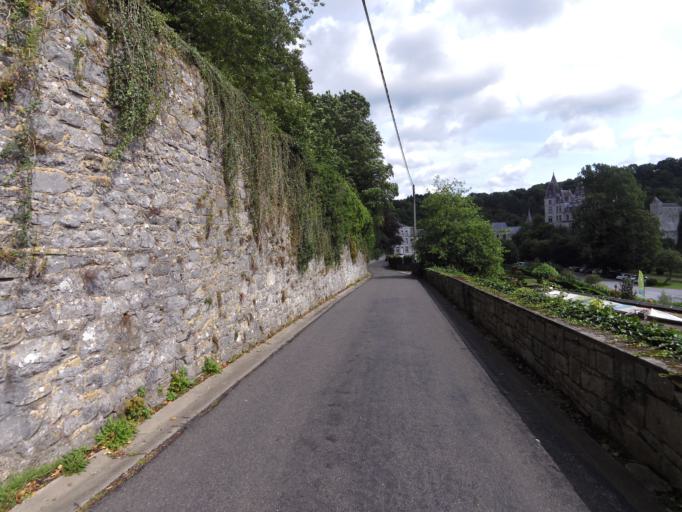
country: BE
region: Wallonia
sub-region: Province du Luxembourg
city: Durbuy
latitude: 50.3530
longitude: 5.4528
